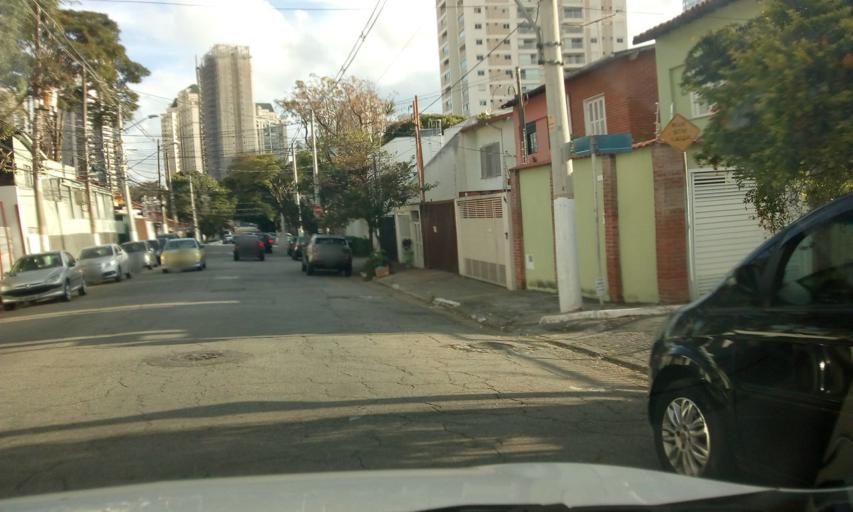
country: BR
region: Sao Paulo
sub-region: Sao Paulo
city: Sao Paulo
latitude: -23.6166
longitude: -46.6935
